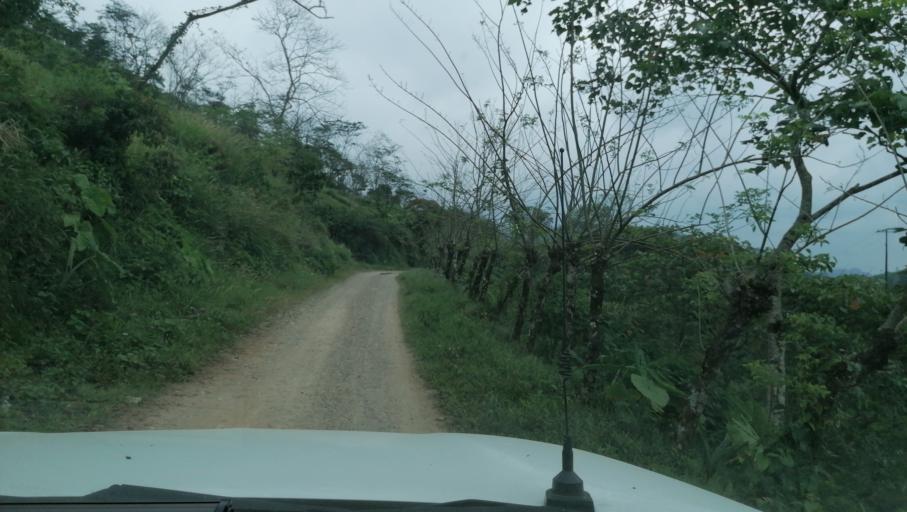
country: MX
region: Chiapas
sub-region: Francisco Leon
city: San Miguel la Sardina
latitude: 17.3382
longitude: -93.3134
